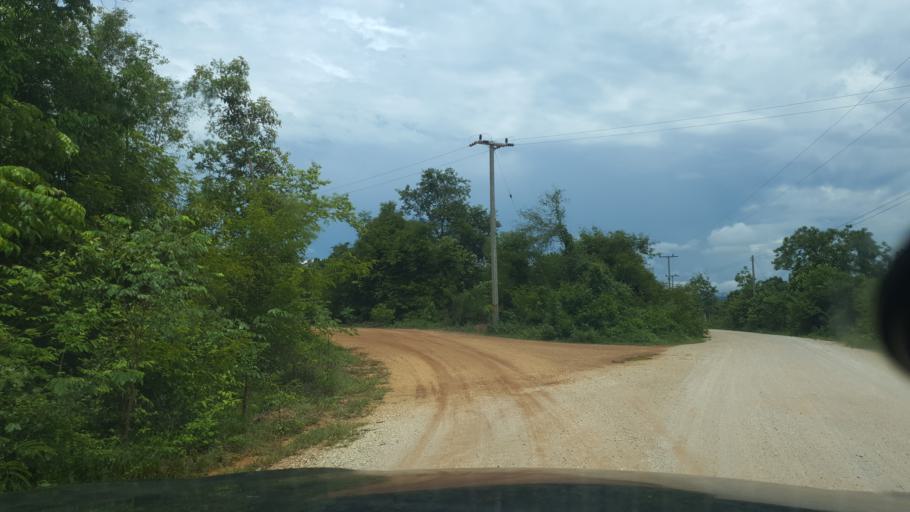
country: TH
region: Lampang
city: Ko Kha
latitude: 18.1874
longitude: 99.3169
